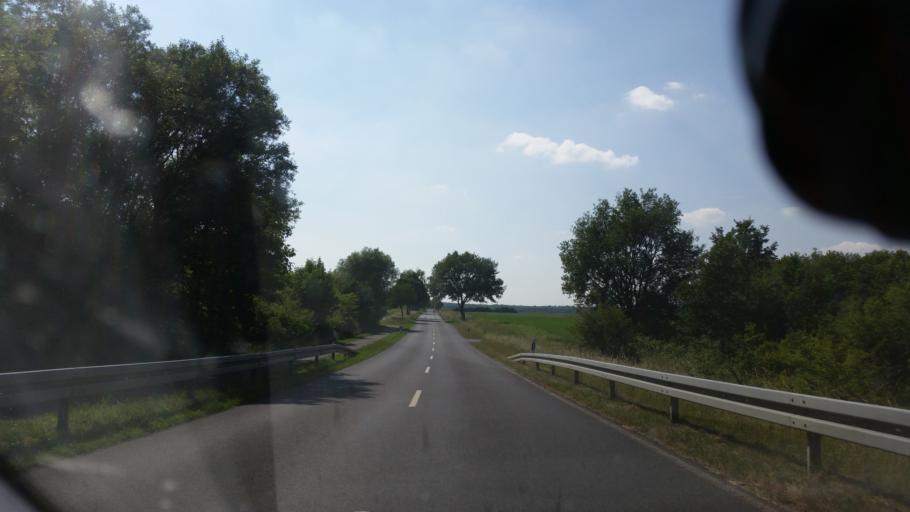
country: DE
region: Lower Saxony
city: Konigslutter am Elm
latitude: 52.3129
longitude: 10.7574
